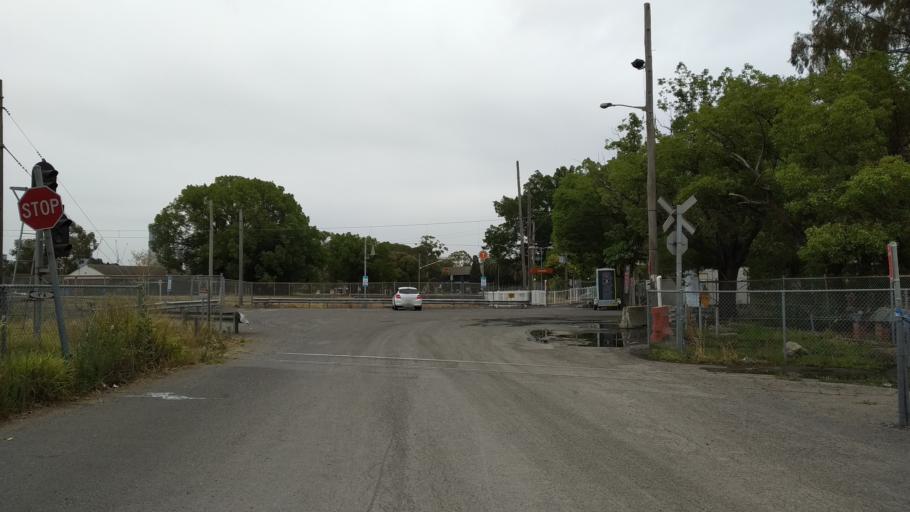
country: AU
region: New South Wales
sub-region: Parramatta
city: Granville
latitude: -33.8195
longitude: 151.0246
